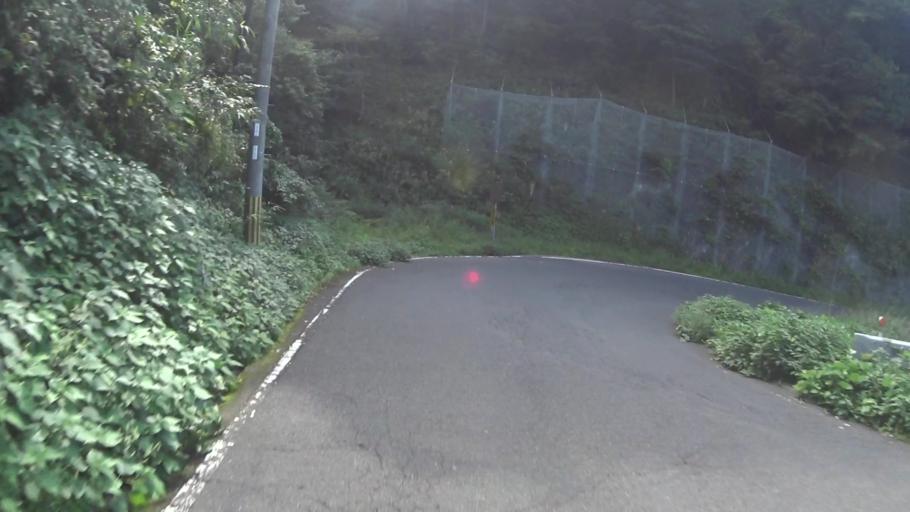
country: JP
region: Kyoto
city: Miyazu
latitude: 35.7691
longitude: 135.2242
